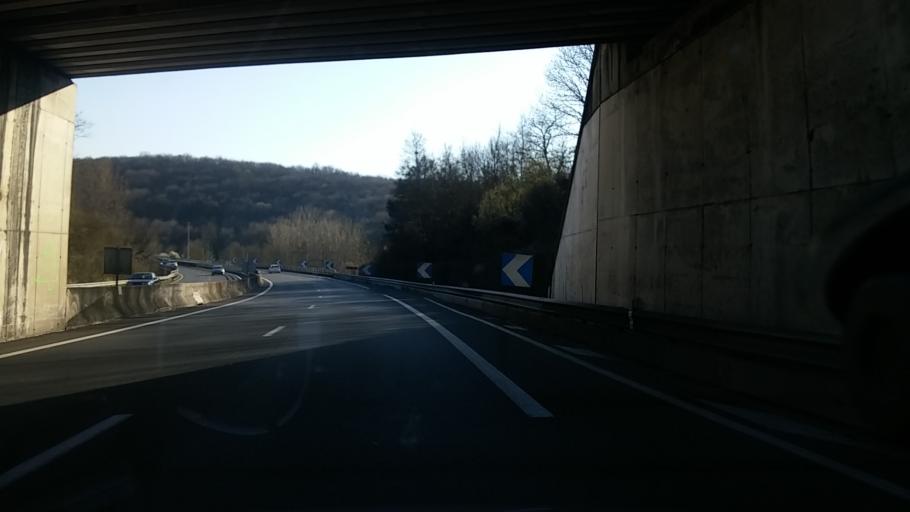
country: FR
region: Centre
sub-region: Departement de l'Indre
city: Saint-Marcel
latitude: 46.6037
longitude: 1.4996
